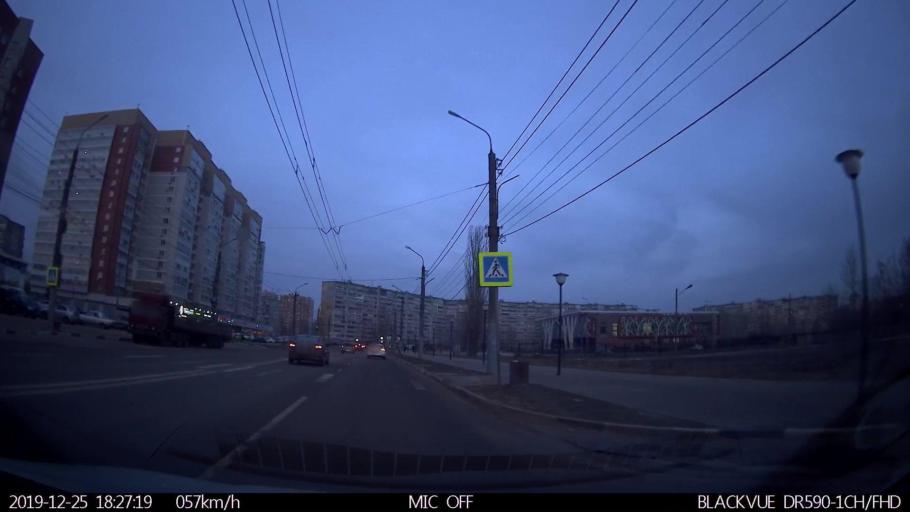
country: RU
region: Nizjnij Novgorod
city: Nizhniy Novgorod
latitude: 56.3397
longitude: 43.9328
